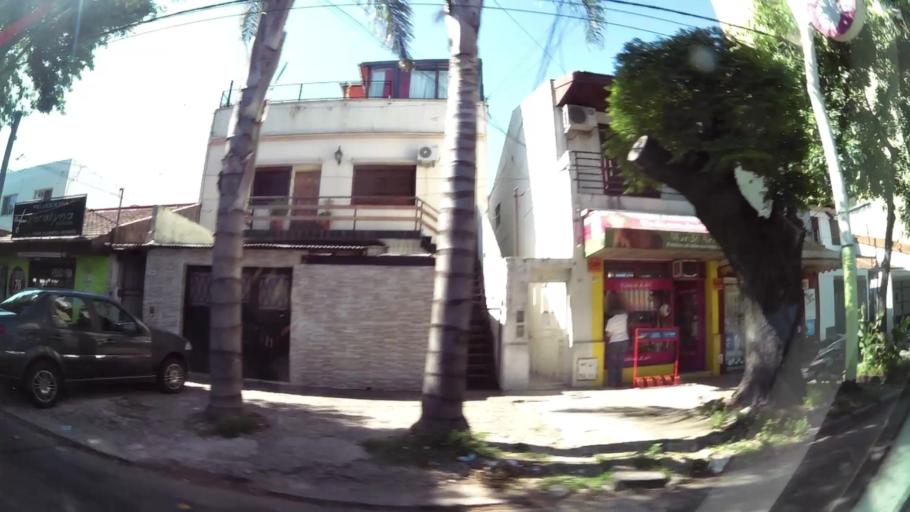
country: AR
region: Buenos Aires
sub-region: Partido de Vicente Lopez
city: Olivos
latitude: -34.5409
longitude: -58.4892
